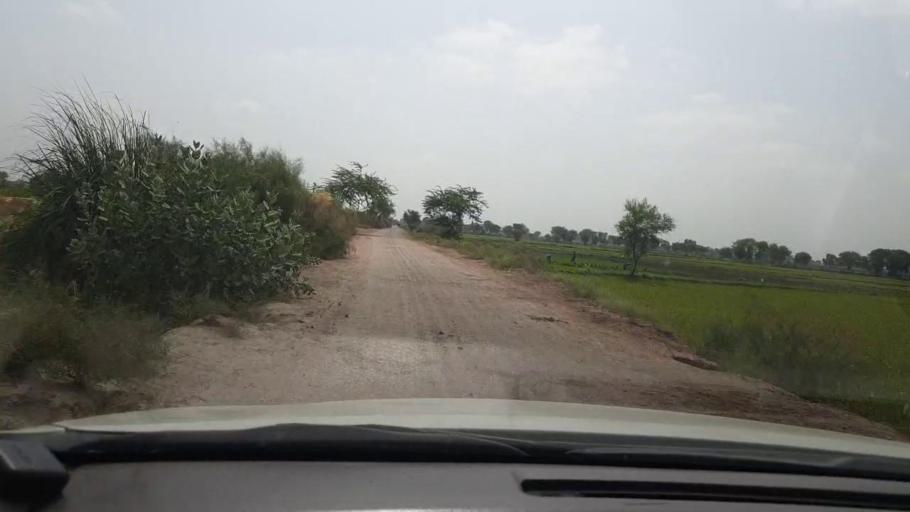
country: PK
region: Sindh
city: Shikarpur
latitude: 28.0078
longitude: 68.5756
